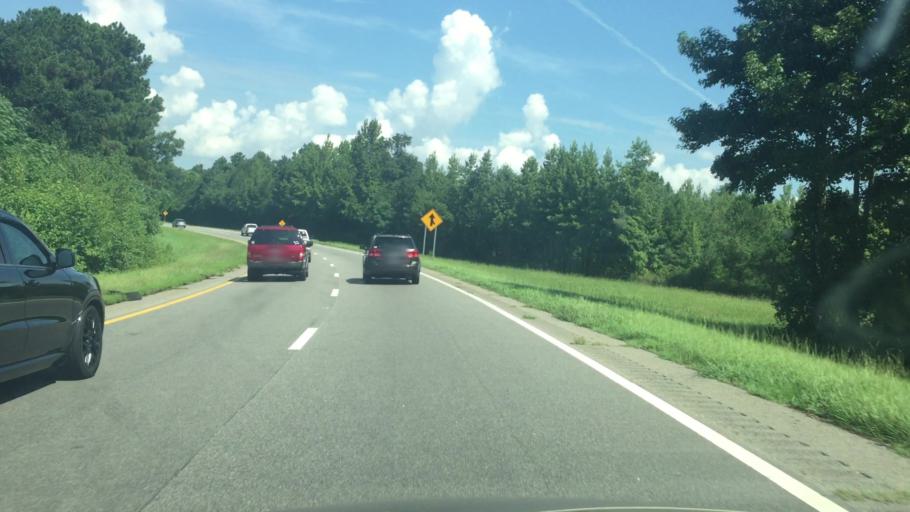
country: US
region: North Carolina
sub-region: Scotland County
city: Laurinburg
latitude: 34.7876
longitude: -79.5043
